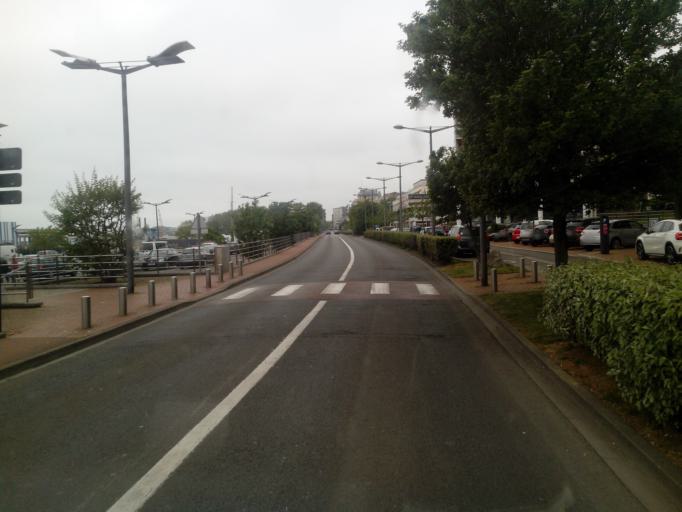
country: FR
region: Nord-Pas-de-Calais
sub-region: Departement du Pas-de-Calais
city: Saint-Martin-Boulogne
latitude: 50.7251
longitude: 1.6011
